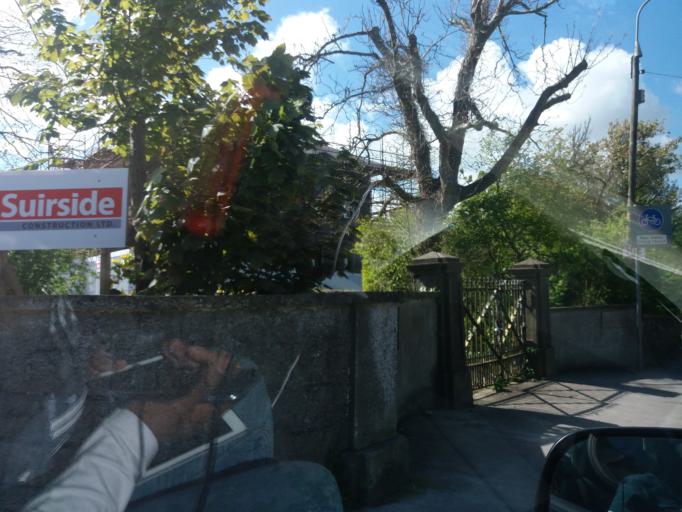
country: IE
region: Munster
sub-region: Waterford
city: Waterford
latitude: 52.2500
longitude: -7.0950
